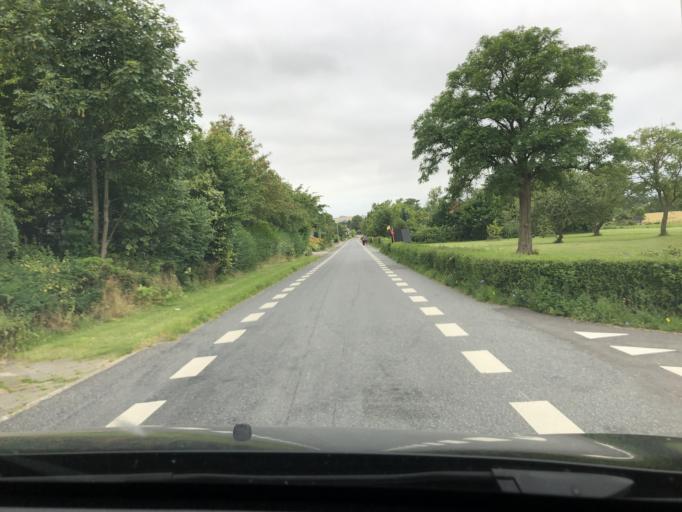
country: DK
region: South Denmark
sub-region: AEro Kommune
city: Marstal
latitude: 54.8551
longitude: 10.4967
